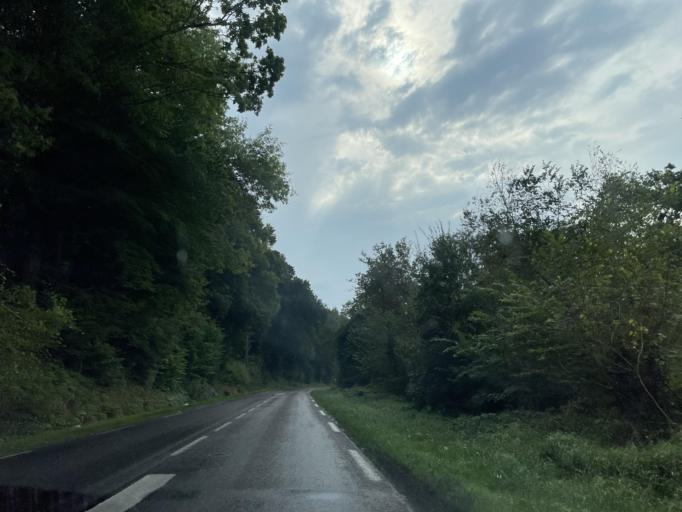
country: FR
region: Haute-Normandie
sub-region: Departement de la Seine-Maritime
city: Neufchatel-en-Bray
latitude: 49.7587
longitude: 1.4268
